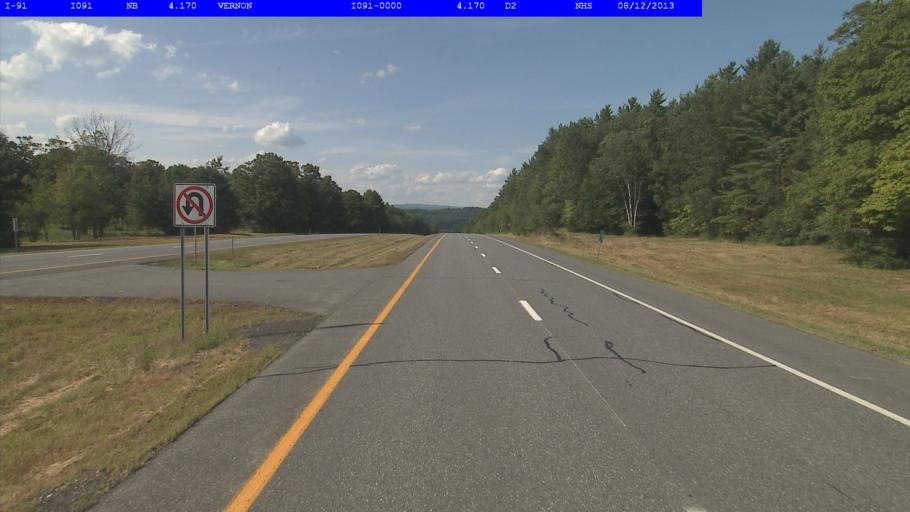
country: US
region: Vermont
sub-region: Windham County
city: Brattleboro
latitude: 42.7899
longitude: -72.5607
